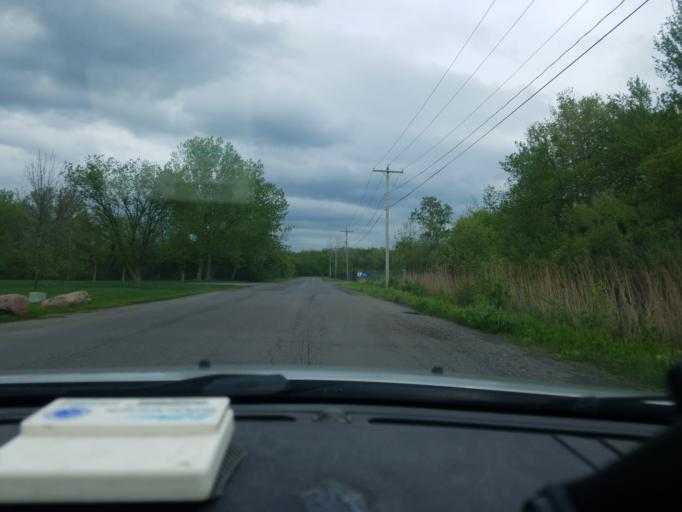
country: US
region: New York
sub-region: Onondaga County
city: Liverpool
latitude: 43.1172
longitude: -76.2010
